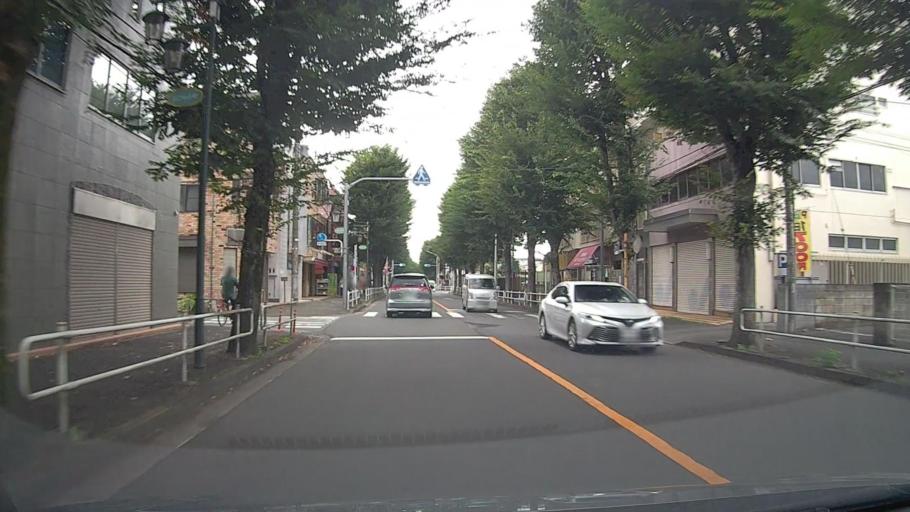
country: JP
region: Tokyo
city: Tanashicho
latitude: 35.7422
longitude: 139.5125
